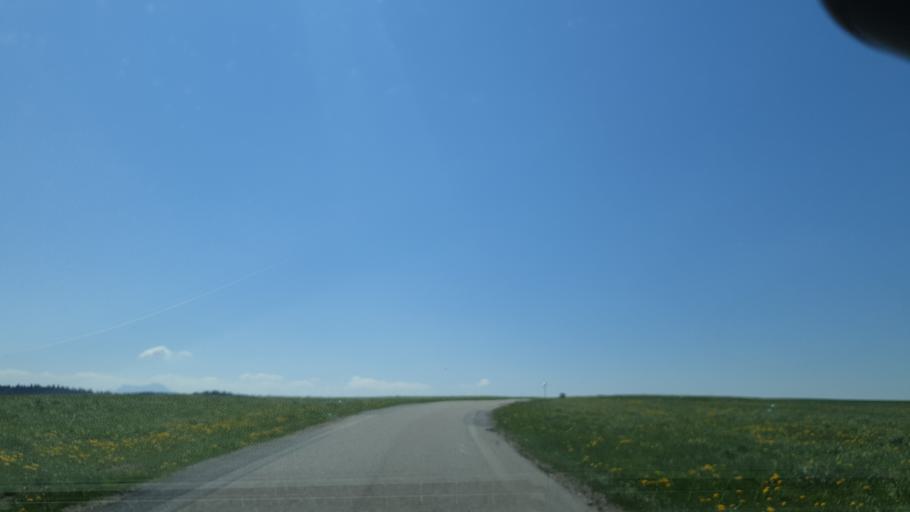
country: AT
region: Upper Austria
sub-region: Politischer Bezirk Vocklabruck
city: Gampern
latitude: 47.9743
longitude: 13.5315
